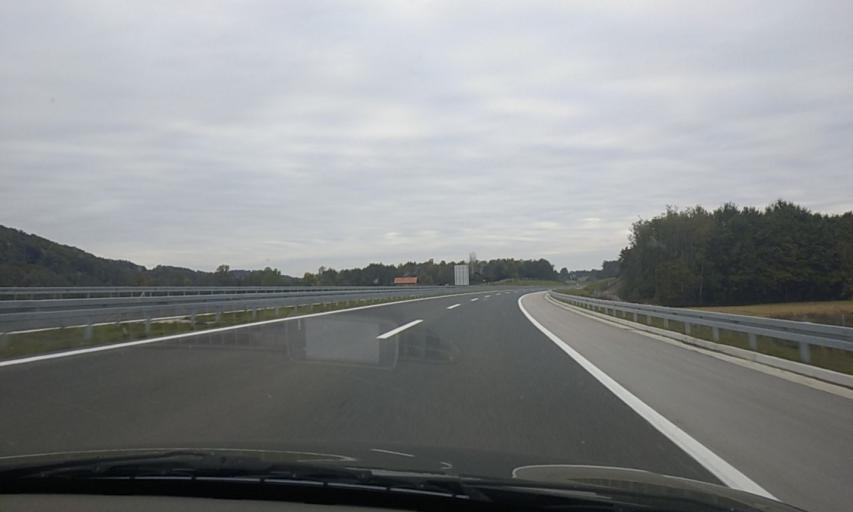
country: BA
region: Republika Srpska
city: Maglajani
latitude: 44.8737
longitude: 17.3911
